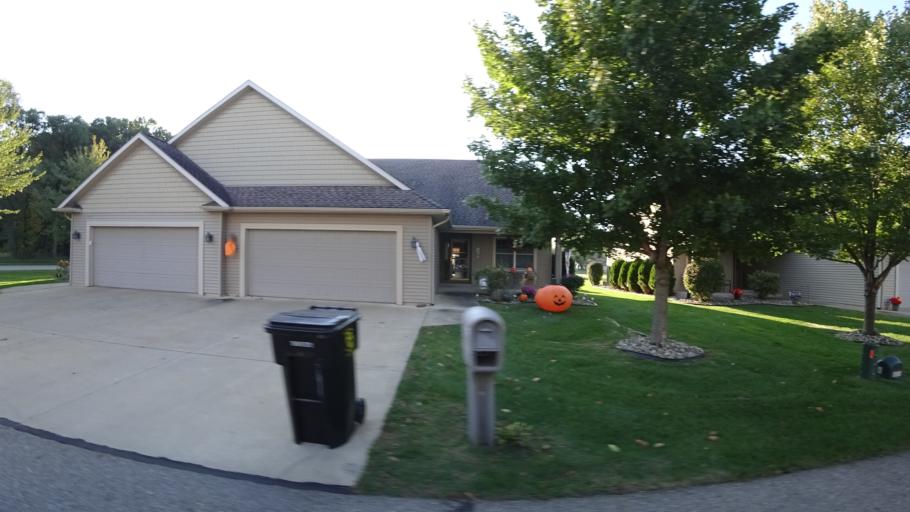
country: US
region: Michigan
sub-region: Saint Joseph County
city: Three Rivers
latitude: 41.9651
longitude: -85.6320
